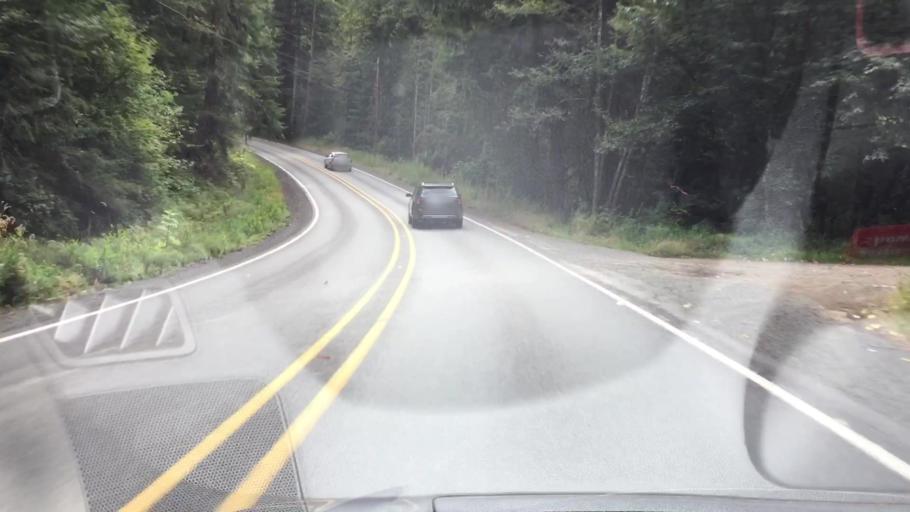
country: US
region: Washington
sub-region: Pierce County
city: Eatonville
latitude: 46.8378
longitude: -122.2516
